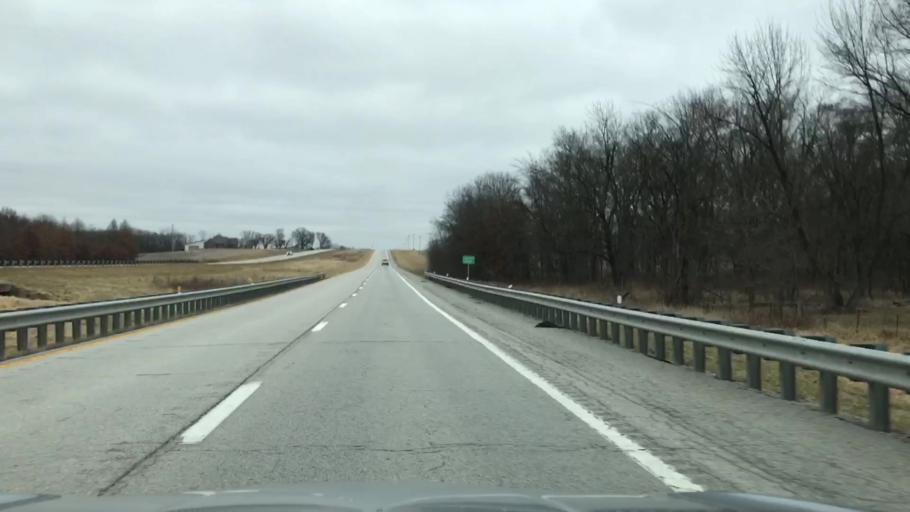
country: US
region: Missouri
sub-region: Linn County
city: Linneus
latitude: 39.7776
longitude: -93.2673
